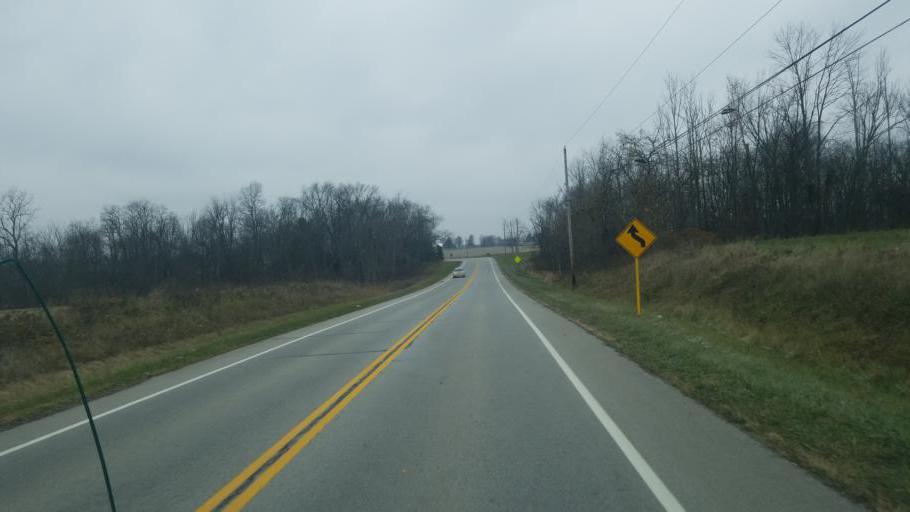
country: US
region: Ohio
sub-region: Medina County
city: Medina
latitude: 41.1473
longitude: -81.9236
